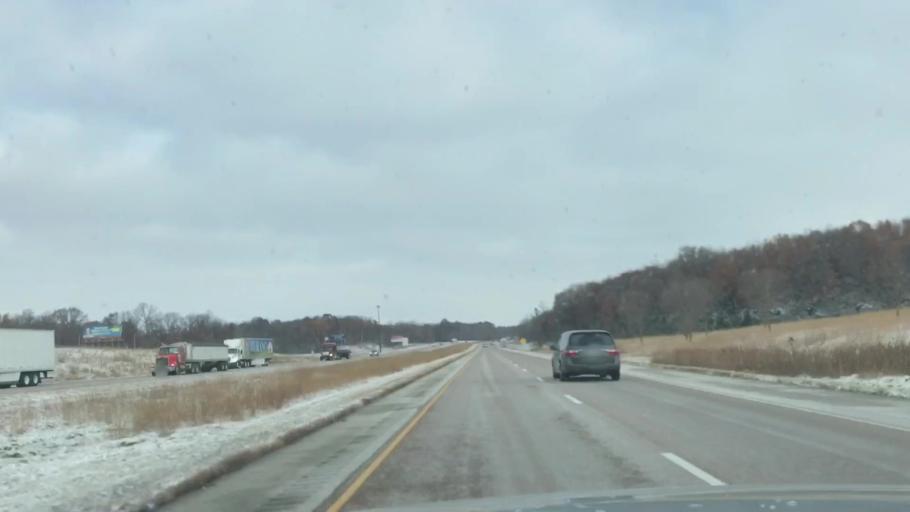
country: US
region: Illinois
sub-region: Macoupin County
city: Mount Olive
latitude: 39.0724
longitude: -89.7556
